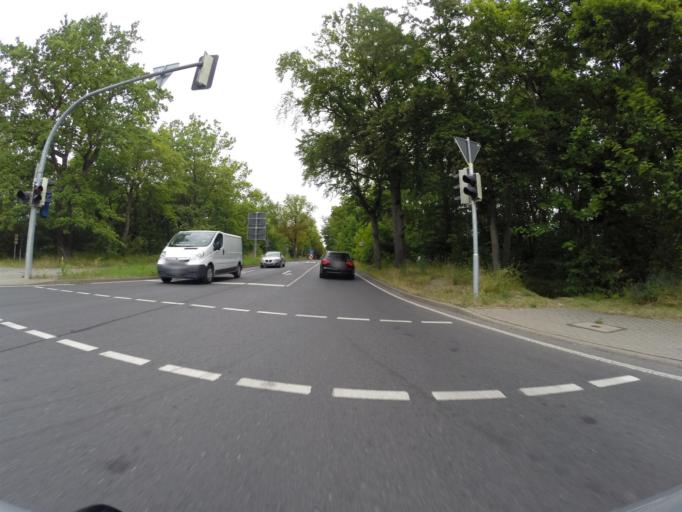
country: DE
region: Thuringia
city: Weimar
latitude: 51.0026
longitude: 11.3124
